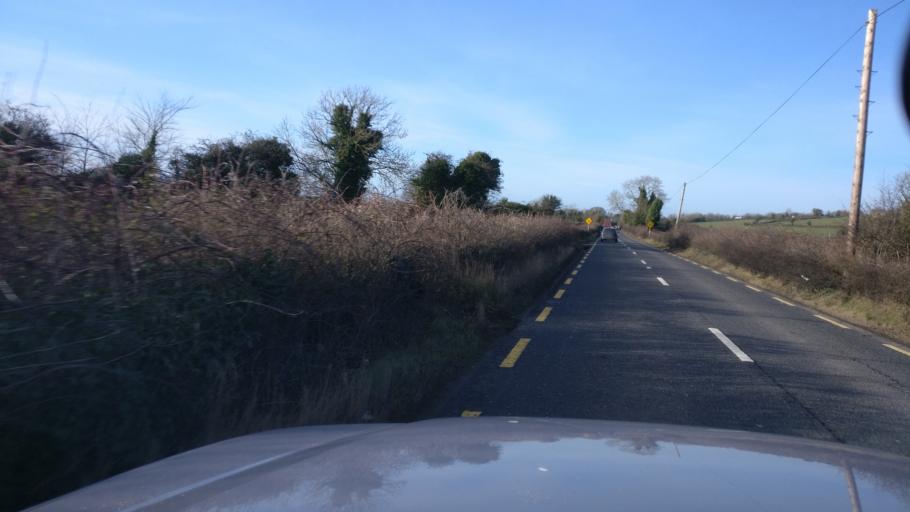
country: IE
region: Leinster
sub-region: Uibh Fhaili
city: Tullamore
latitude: 53.1917
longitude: -7.4098
